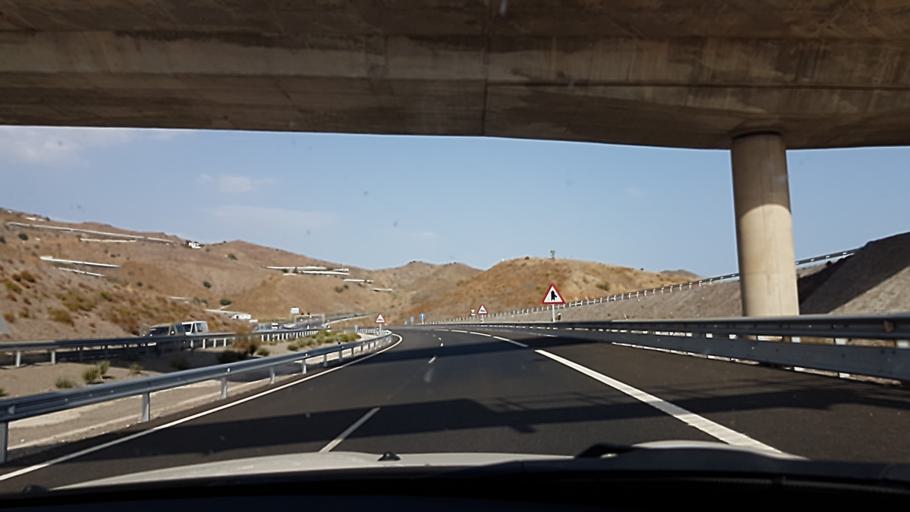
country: ES
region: Andalusia
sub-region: Provincia de Granada
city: Polopos
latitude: 36.7487
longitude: -3.3128
